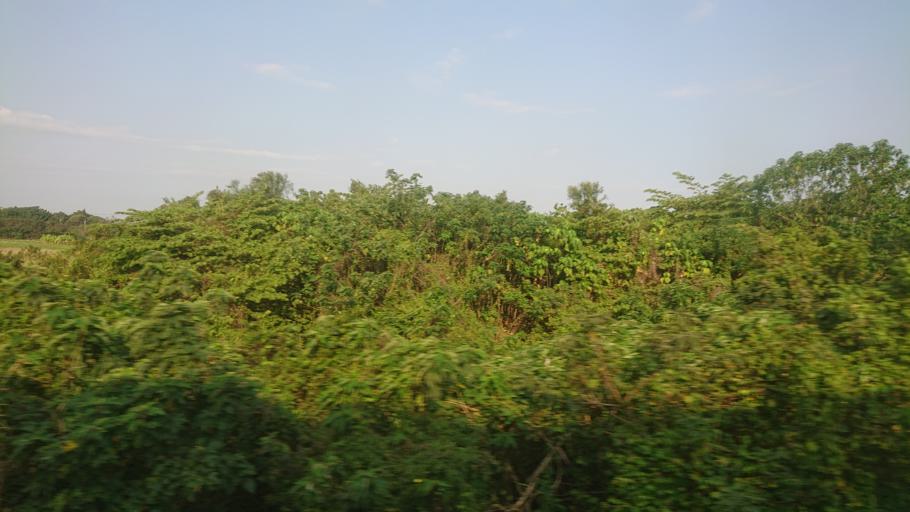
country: TW
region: Taiwan
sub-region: Chiayi
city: Jiayi Shi
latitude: 23.5972
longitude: 120.4522
